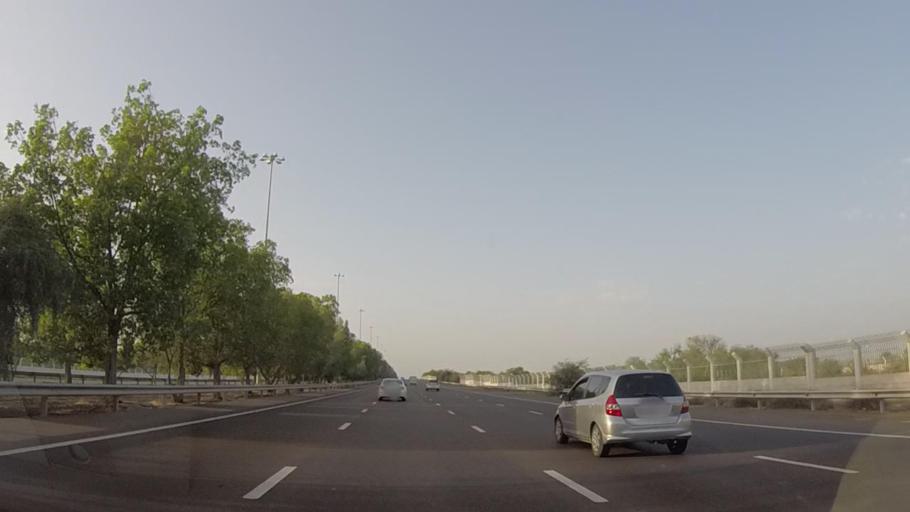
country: AE
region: Dubai
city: Dubai
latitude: 24.8390
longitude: 54.8886
